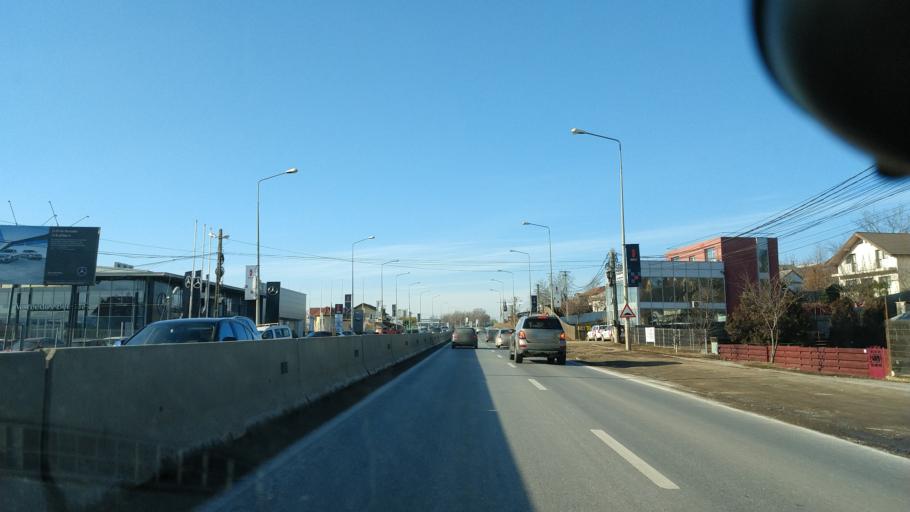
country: RO
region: Iasi
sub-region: Comuna Valea Lupului
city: Valea Lupului
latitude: 47.1747
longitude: 27.5017
